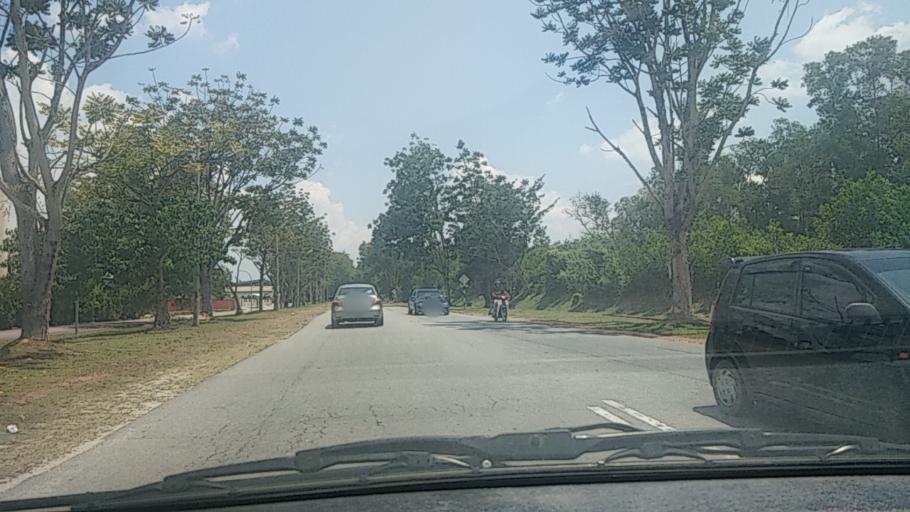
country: MY
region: Kedah
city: Sungai Petani
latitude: 5.6458
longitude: 100.5309
